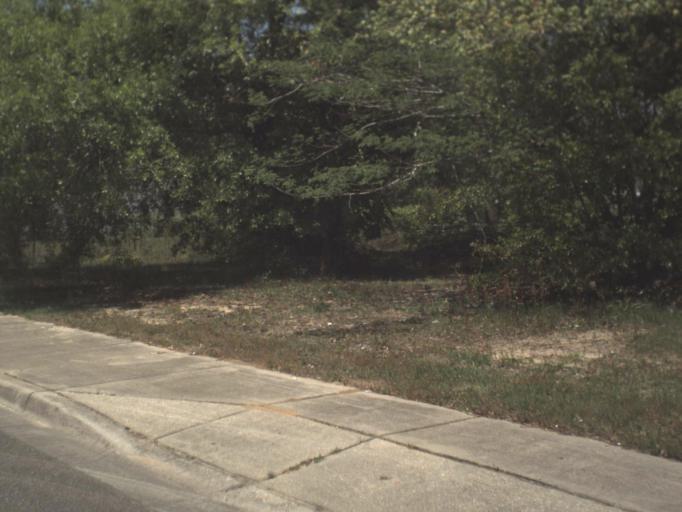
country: US
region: Florida
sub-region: Escambia County
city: Brent
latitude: 30.4767
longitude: -87.2435
